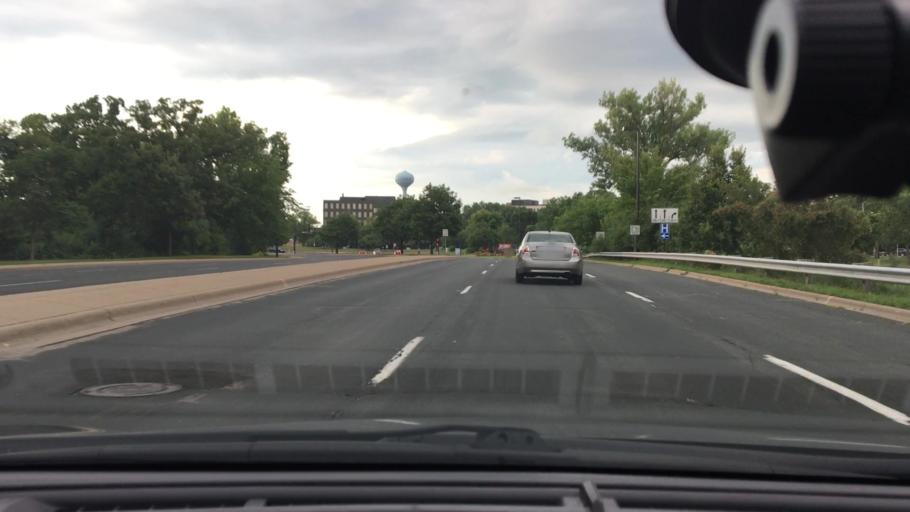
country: US
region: Minnesota
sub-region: Hennepin County
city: Edina
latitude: 44.8854
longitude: -93.3332
